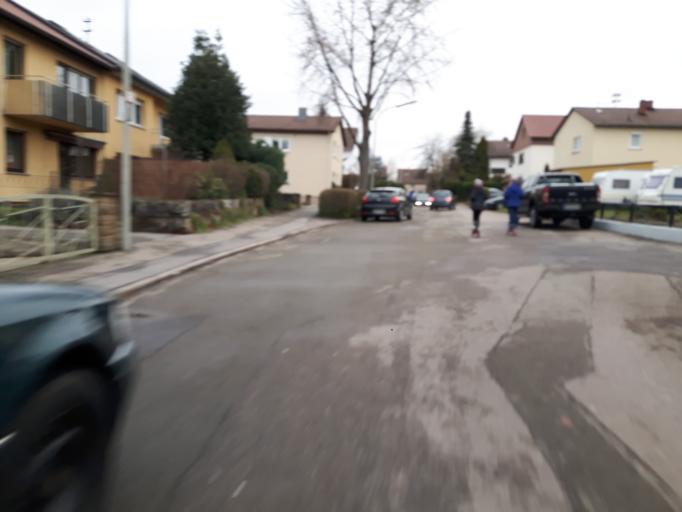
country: DE
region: Baden-Wuerttemberg
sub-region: Regierungsbezirk Stuttgart
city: Flein
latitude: 49.1055
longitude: 9.2073
